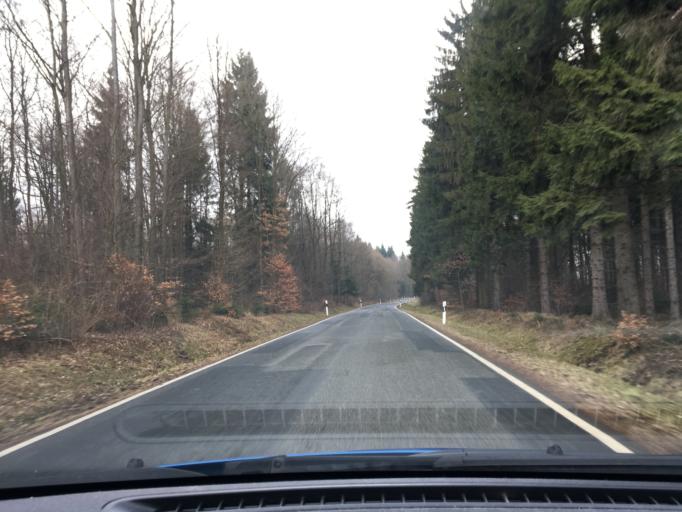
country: DE
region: Lower Saxony
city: Buhren
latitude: 51.5027
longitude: 9.6582
